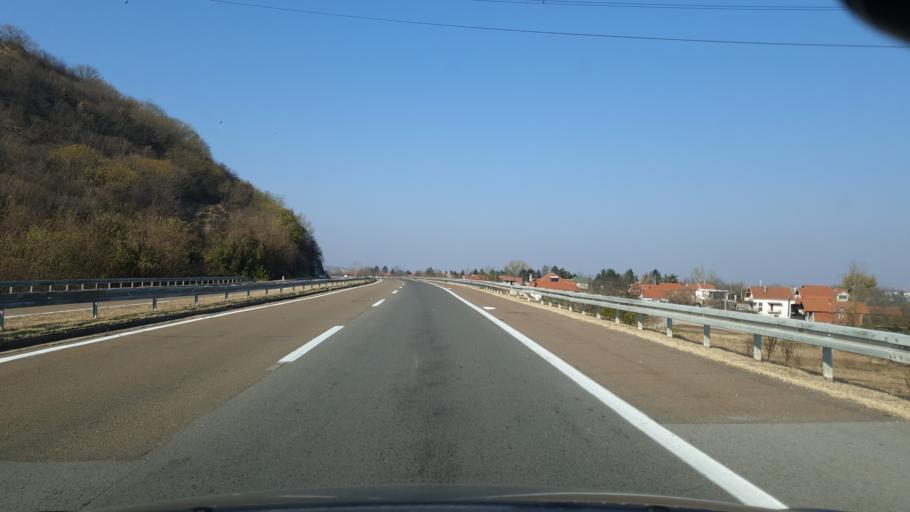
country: RS
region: Central Serbia
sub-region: Nisavski Okrug
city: Doljevac
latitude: 43.2199
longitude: 21.8352
